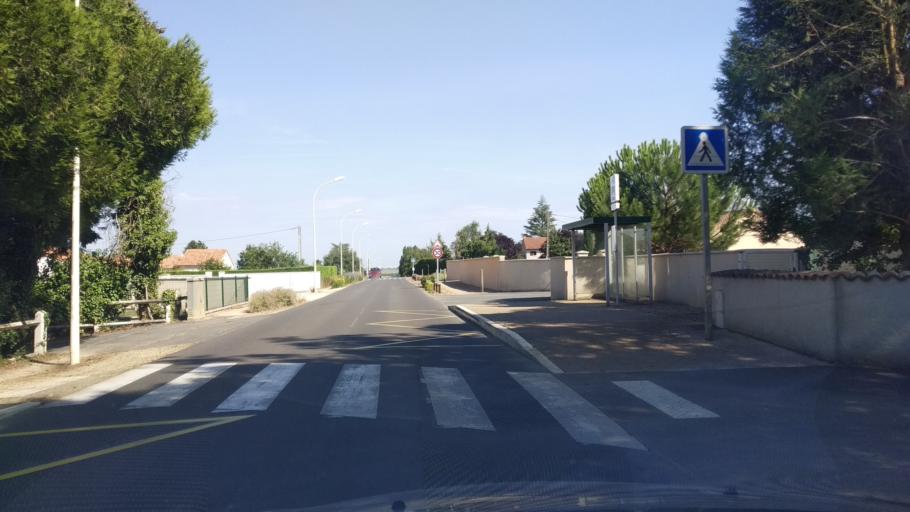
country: FR
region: Poitou-Charentes
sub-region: Departement de la Vienne
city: Cisse
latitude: 46.6370
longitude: 0.2440
